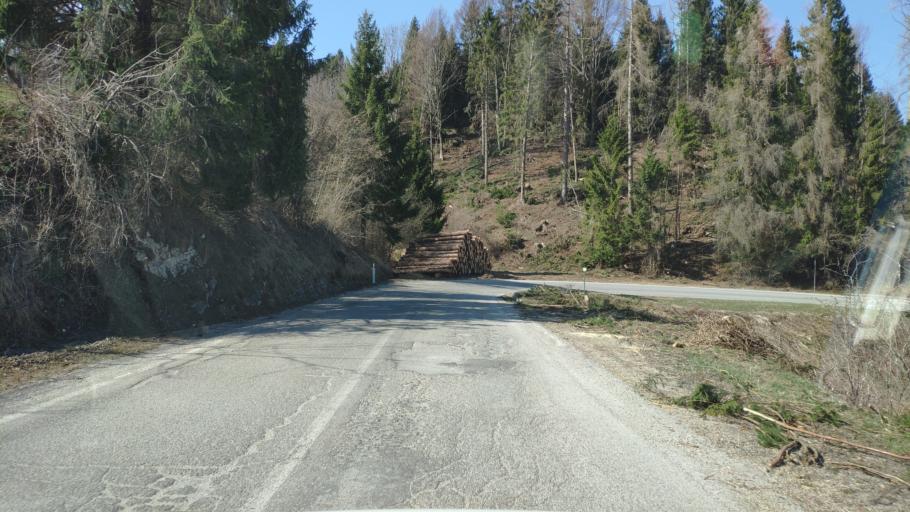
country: IT
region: Veneto
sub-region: Provincia di Vicenza
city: Enego
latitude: 45.9300
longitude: 11.7034
